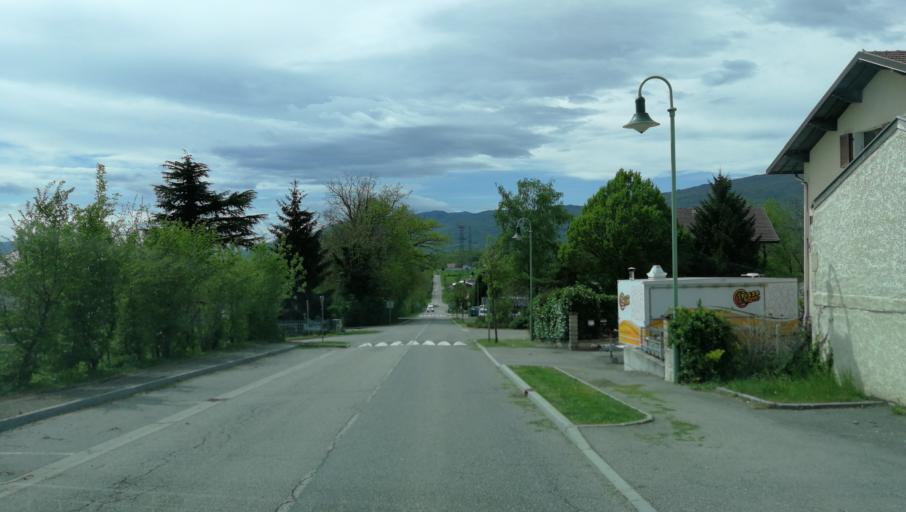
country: FR
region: Rhone-Alpes
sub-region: Departement de l'Ain
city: Bellegarde-sur-Valserine
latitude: 46.0753
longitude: 5.7837
